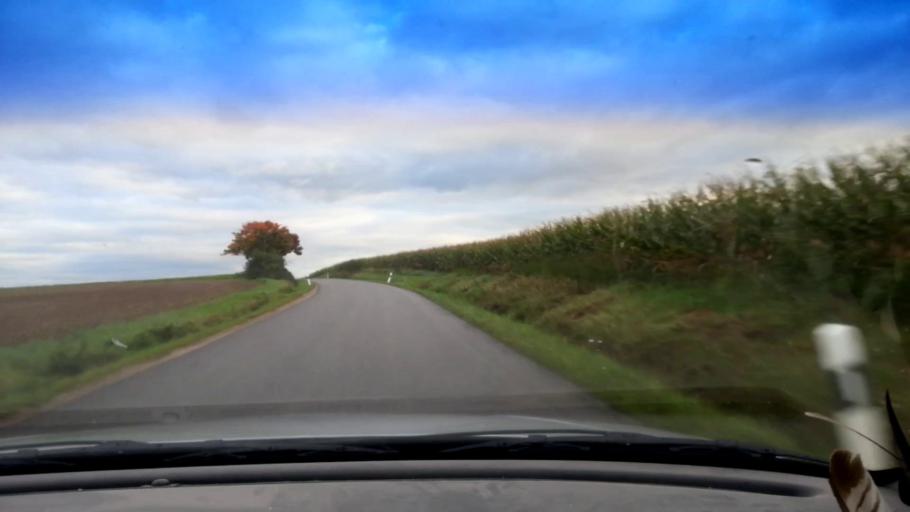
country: DE
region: Bavaria
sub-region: Upper Franconia
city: Burgebrach
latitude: 49.8162
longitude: 10.6852
